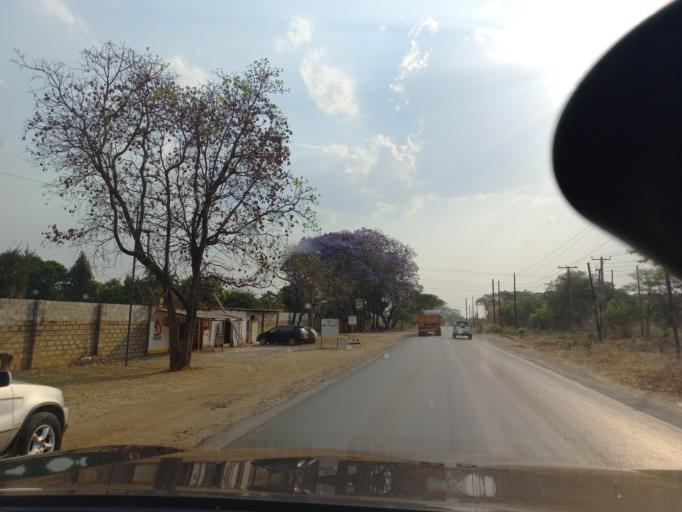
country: ZM
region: Lusaka
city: Lusaka
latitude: -15.4762
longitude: 28.2112
